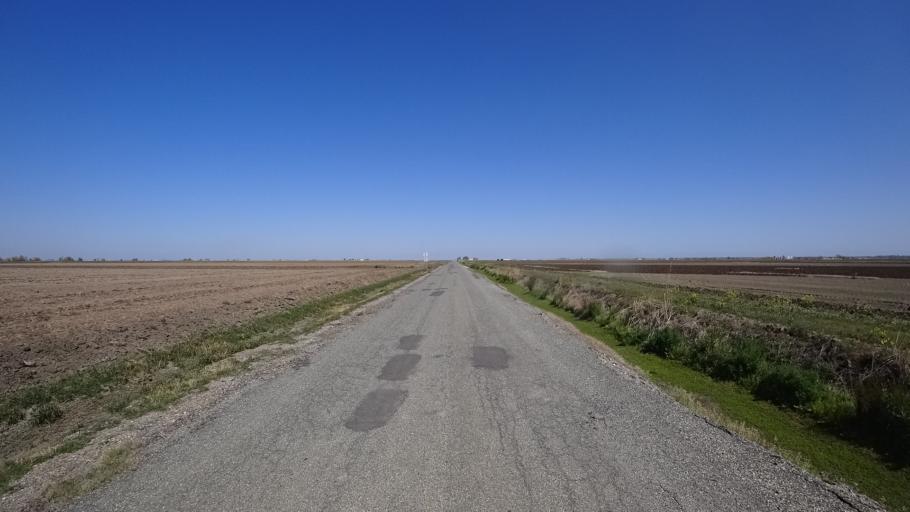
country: US
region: California
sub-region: Glenn County
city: Willows
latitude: 39.4295
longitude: -122.0651
